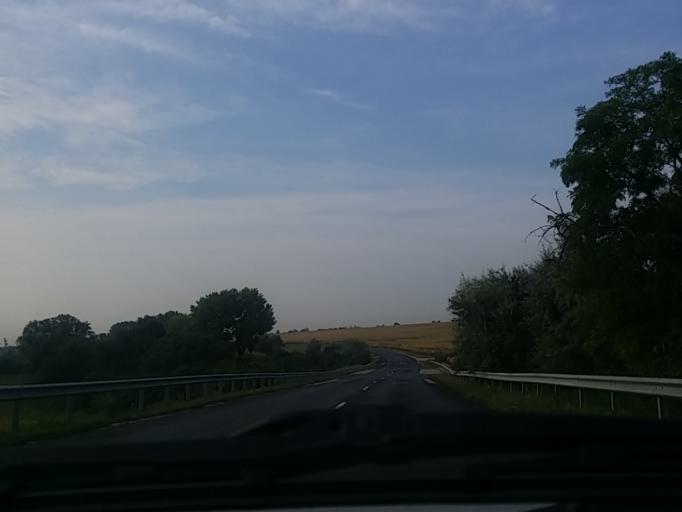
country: HU
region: Fejer
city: Bicske
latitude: 47.4822
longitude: 18.5753
